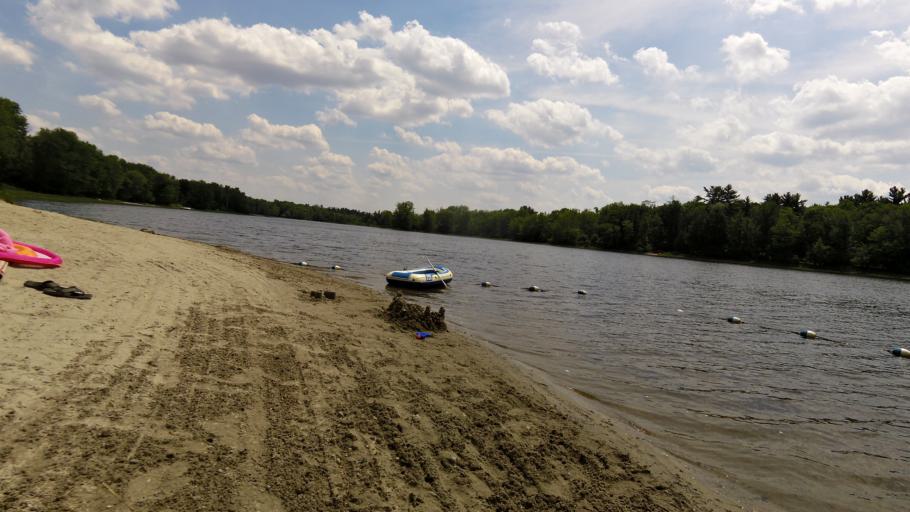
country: CA
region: Ontario
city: Arnprior
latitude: 45.4752
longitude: -76.2224
